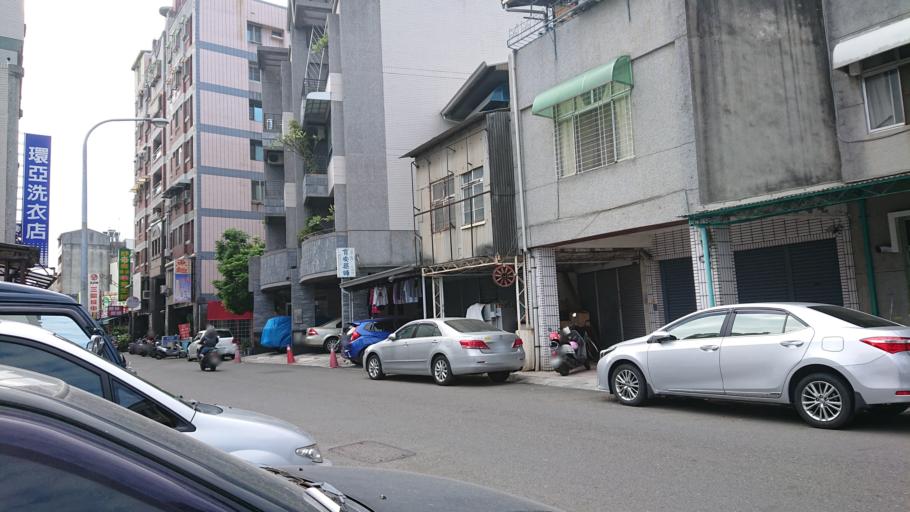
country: TW
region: Taiwan
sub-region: Tainan
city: Tainan
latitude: 23.0031
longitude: 120.2048
